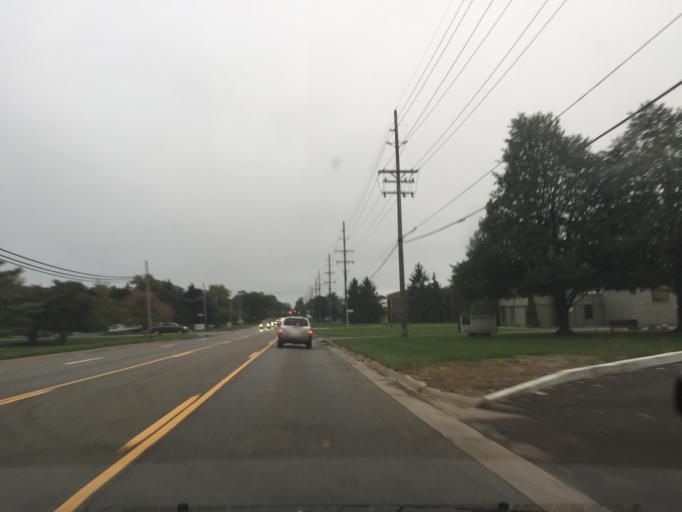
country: US
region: Michigan
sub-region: Oakland County
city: Pontiac
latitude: 42.6067
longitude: -83.2876
